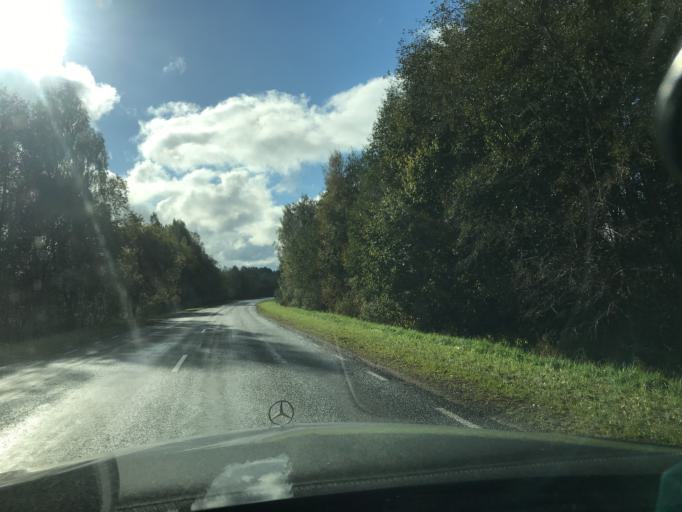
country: EE
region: Tartu
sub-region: Elva linn
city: Elva
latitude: 58.0022
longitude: 26.2679
